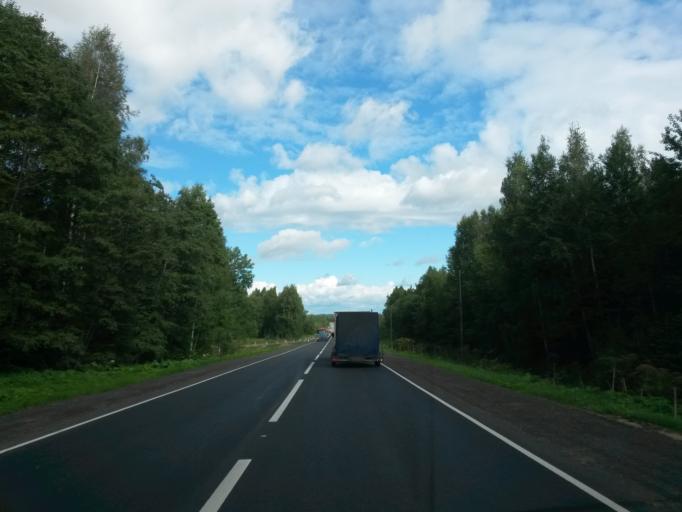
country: RU
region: Jaroslavl
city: Yaroslavl
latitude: 57.5036
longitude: 39.8986
